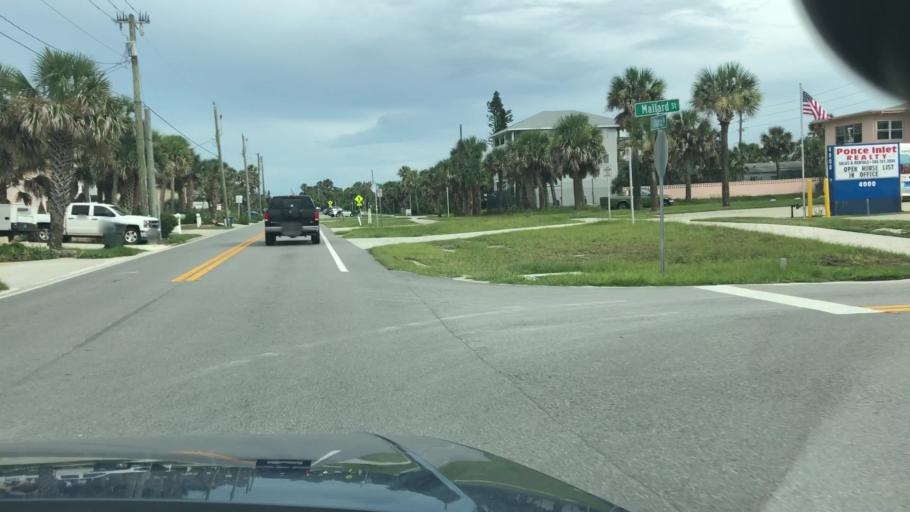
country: US
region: Florida
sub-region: Volusia County
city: Port Orange
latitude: 29.1331
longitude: -80.9587
